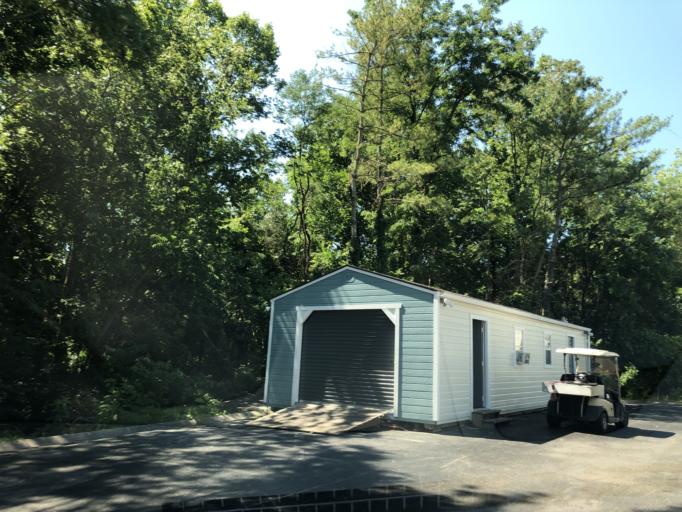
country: US
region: Tennessee
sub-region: Rutherford County
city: La Vergne
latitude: 36.0414
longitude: -86.6657
